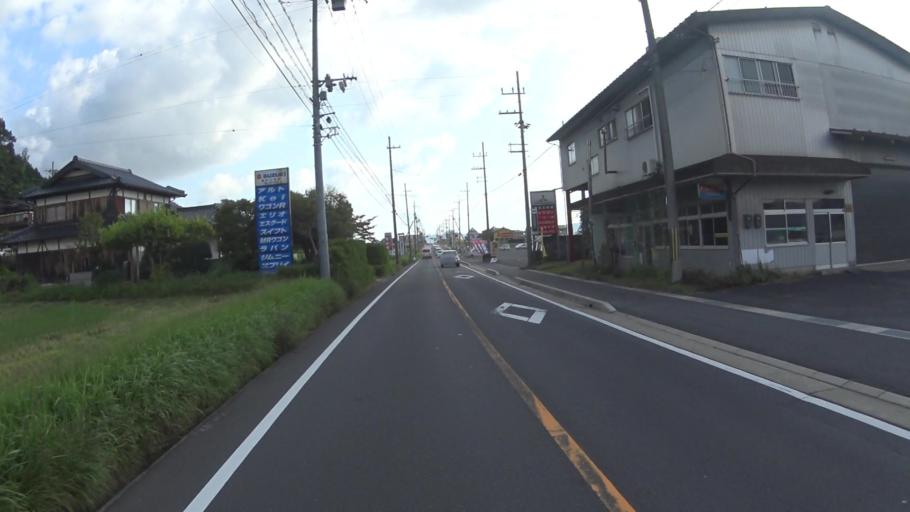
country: JP
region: Kyoto
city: Miyazu
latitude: 35.5750
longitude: 135.1736
